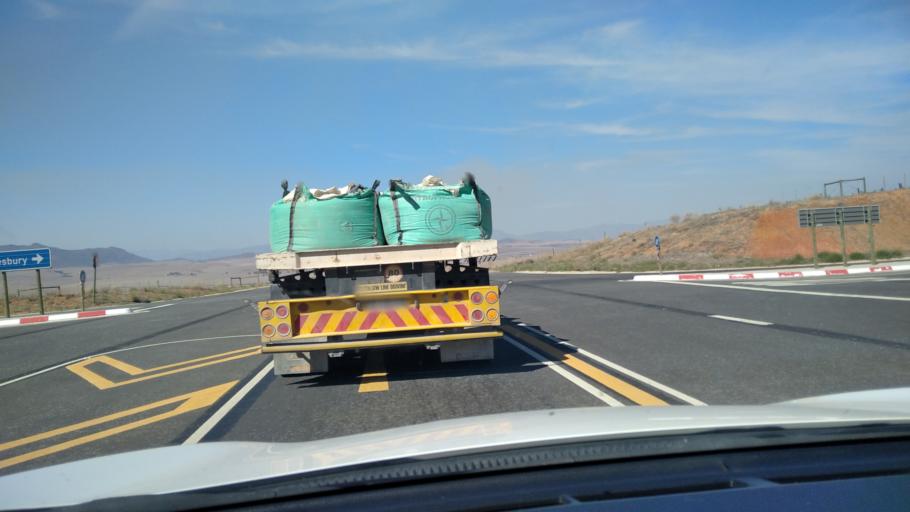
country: ZA
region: Western Cape
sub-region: West Coast District Municipality
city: Malmesbury
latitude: -33.4140
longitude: 18.7139
